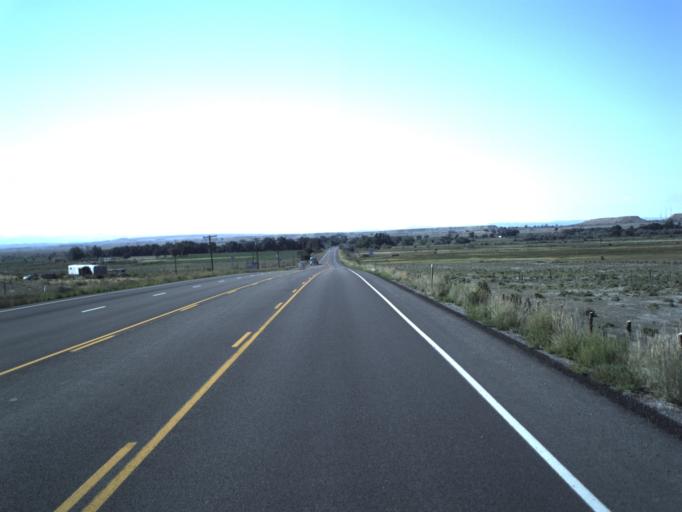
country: US
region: Utah
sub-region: Emery County
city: Huntington
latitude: 39.3172
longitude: -110.9645
